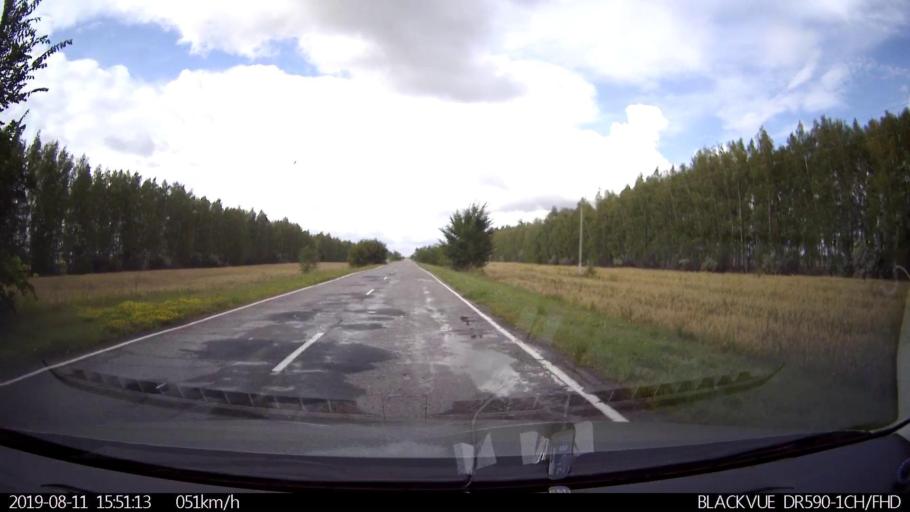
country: RU
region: Ulyanovsk
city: Ignatovka
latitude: 53.9171
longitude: 47.6560
